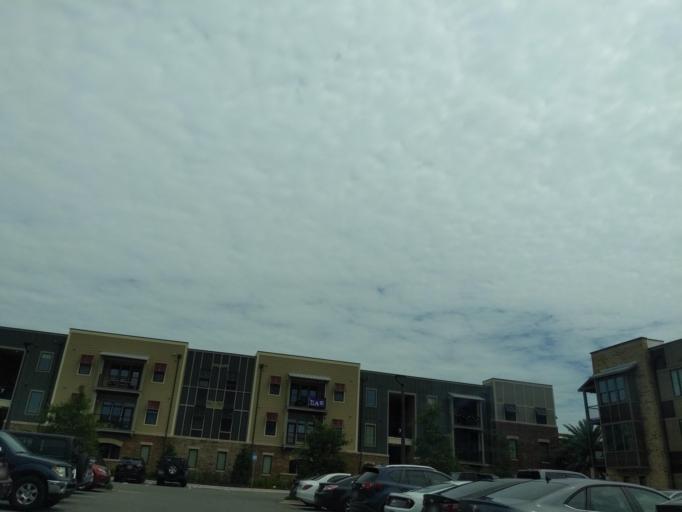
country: US
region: Florida
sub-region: Leon County
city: Tallahassee
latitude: 30.4334
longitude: -84.2979
